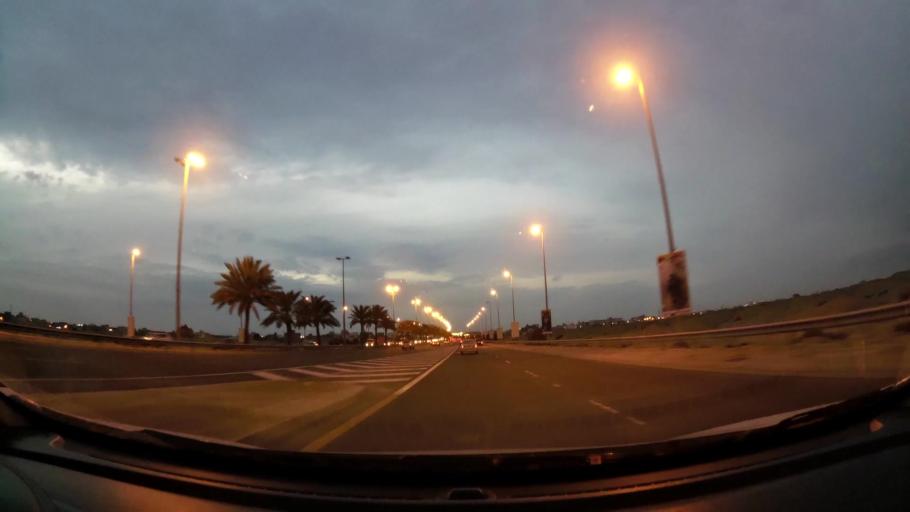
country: BH
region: Central Governorate
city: Madinat Hamad
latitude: 26.1457
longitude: 50.5100
